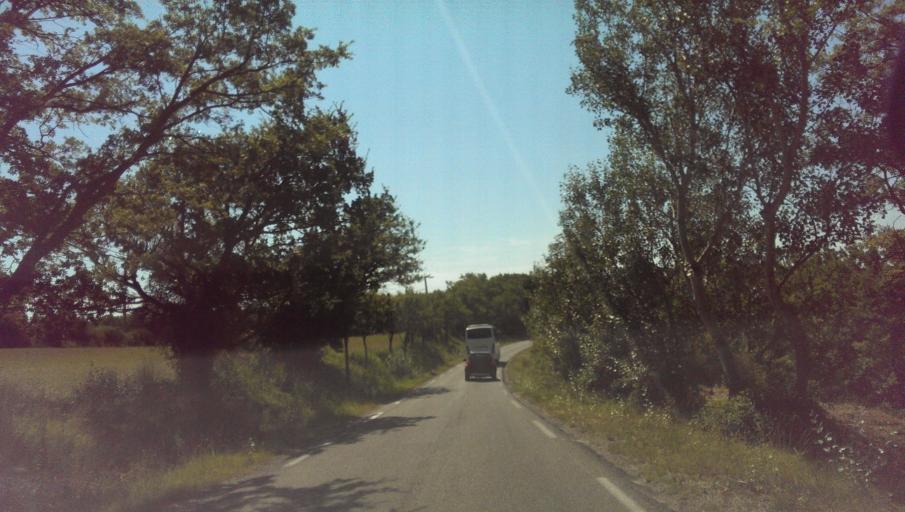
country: FR
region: Provence-Alpes-Cote d'Azur
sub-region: Departement du Vaucluse
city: Gordes
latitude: 43.9482
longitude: 5.2106
